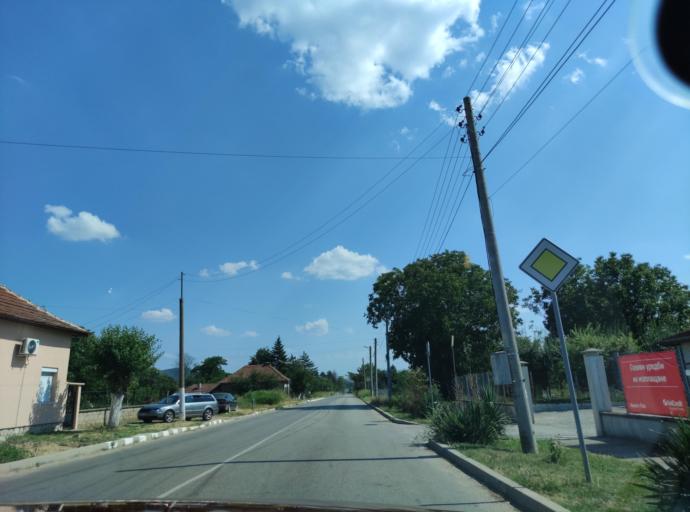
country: BG
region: Pleven
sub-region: Obshtina Cherven Bryag
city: Koynare
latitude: 43.3344
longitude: 24.0664
